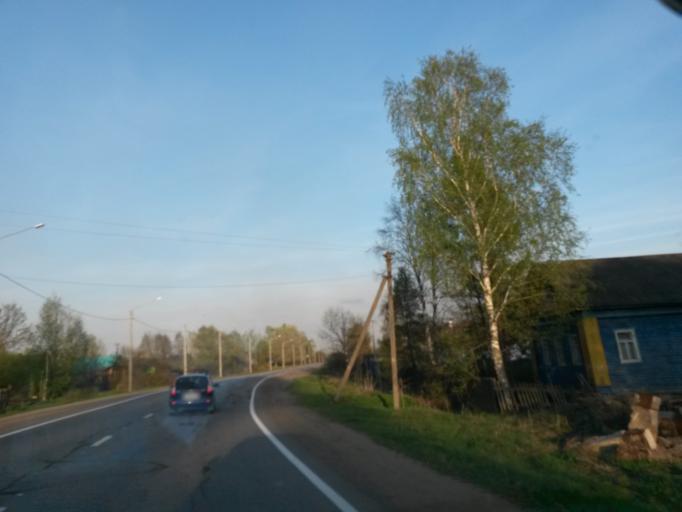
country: RU
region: Jaroslavl
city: Kurba
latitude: 57.6782
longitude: 39.5796
